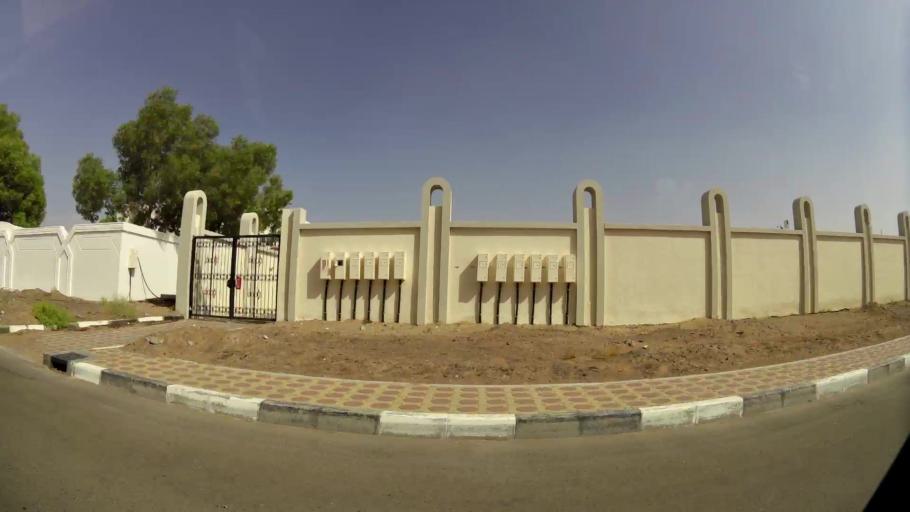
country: AE
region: Abu Dhabi
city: Al Ain
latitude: 24.2399
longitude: 55.6906
